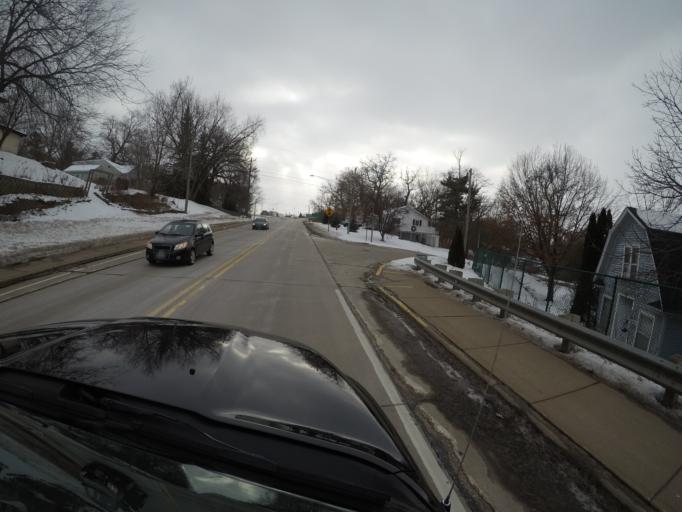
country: US
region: Wisconsin
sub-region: Trempealeau County
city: Galesville
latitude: 44.0797
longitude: -91.3498
